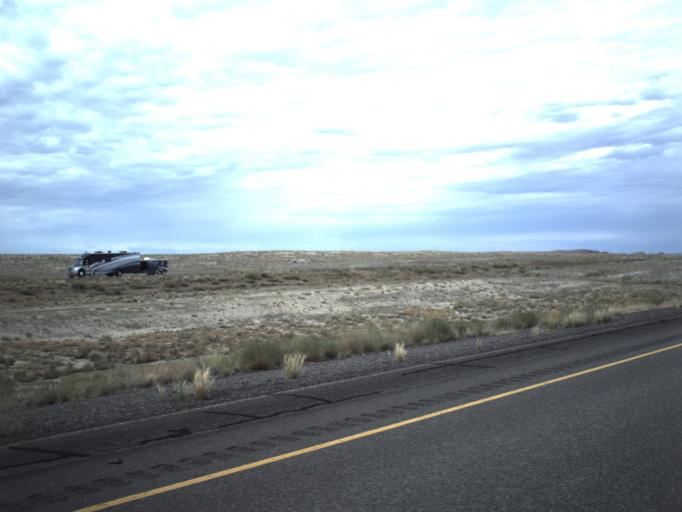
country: US
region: Utah
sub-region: Grand County
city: Moab
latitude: 38.9418
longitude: -109.5531
